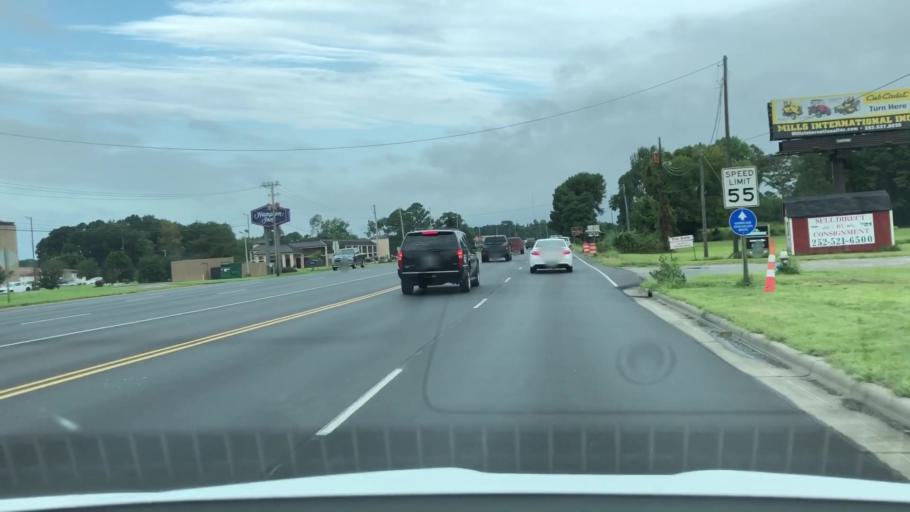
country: US
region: North Carolina
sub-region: Lenoir County
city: Kinston
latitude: 35.2446
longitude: -77.5856
